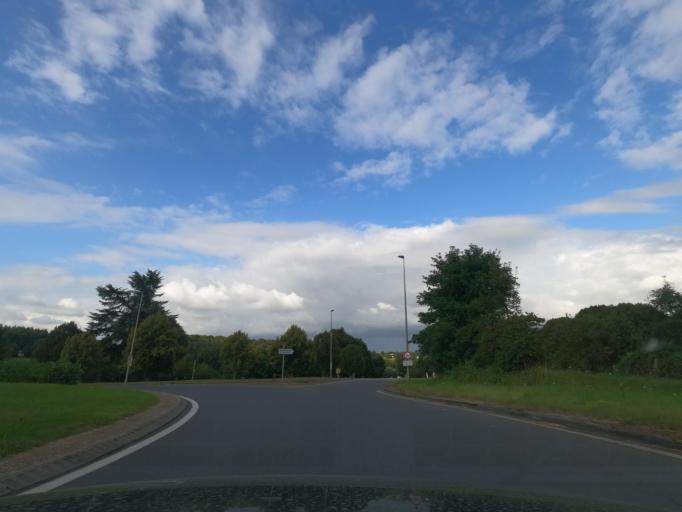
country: FR
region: Haute-Normandie
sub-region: Departement de l'Eure
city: Bernay
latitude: 49.0824
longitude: 0.5742
